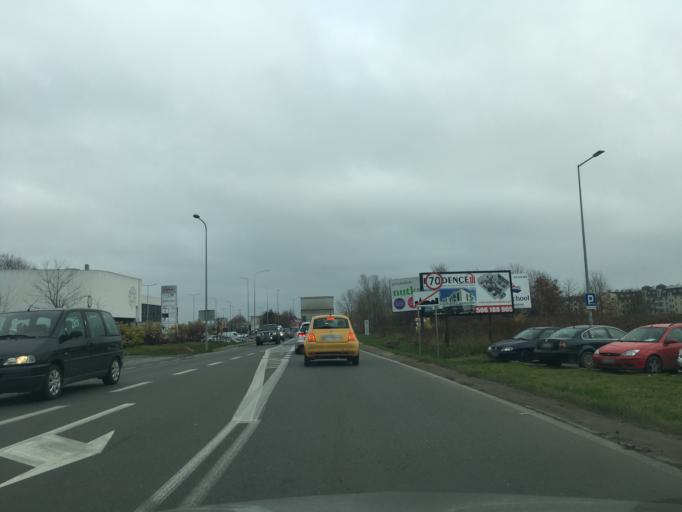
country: PL
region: Masovian Voivodeship
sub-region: Powiat piaseczynski
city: Piaseczno
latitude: 52.0822
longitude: 21.0087
